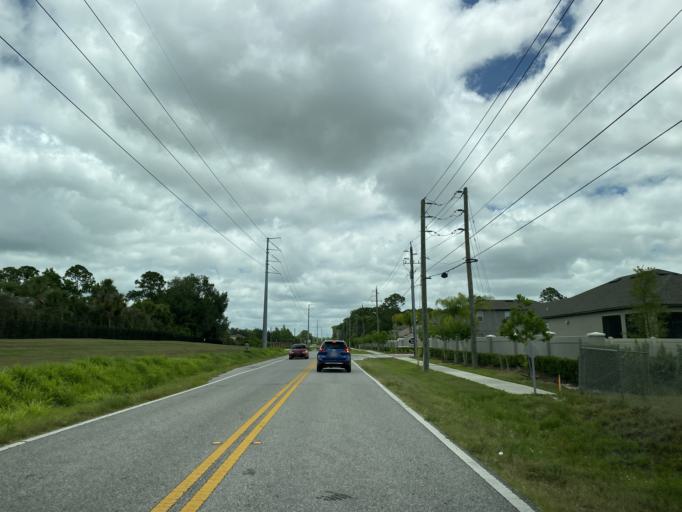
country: US
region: Florida
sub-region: Volusia County
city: DeBary
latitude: 28.8233
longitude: -81.3393
